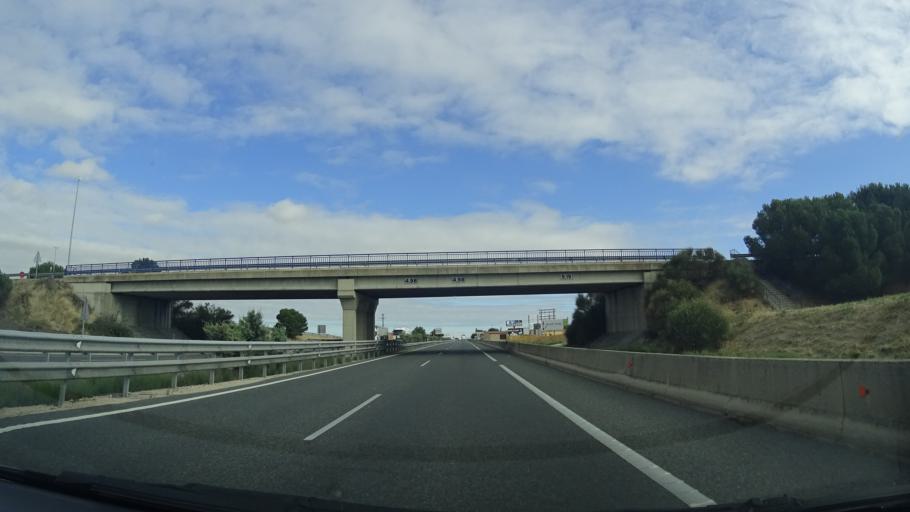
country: ES
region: Castille and Leon
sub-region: Provincia de Valladolid
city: Ataquines
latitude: 41.1769
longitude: -4.8053
